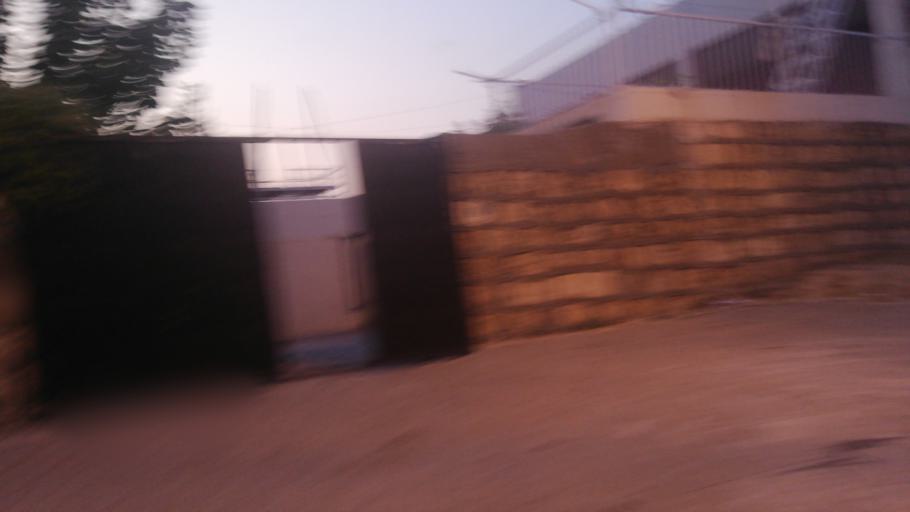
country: TR
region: Mardin
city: Kindirip
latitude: 37.4473
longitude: 41.2251
